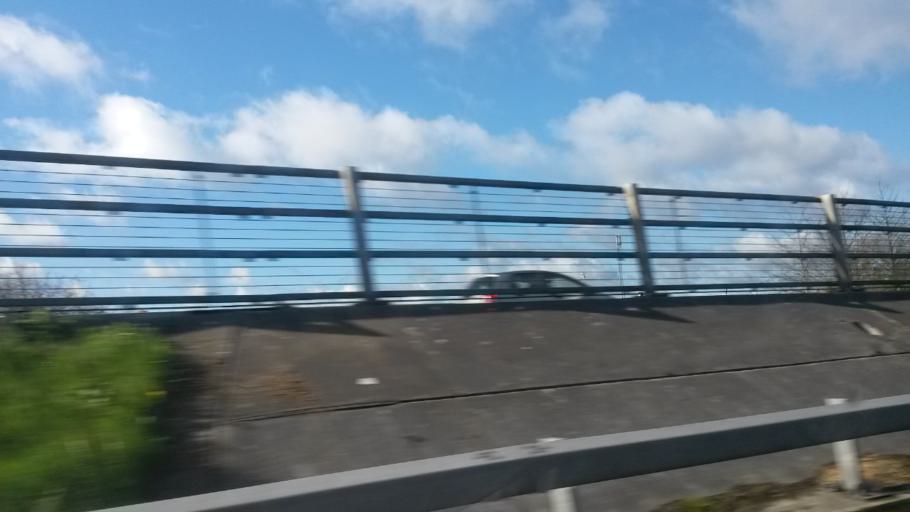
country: IE
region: Munster
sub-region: County Cork
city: Passage West
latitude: 51.9065
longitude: -8.3961
